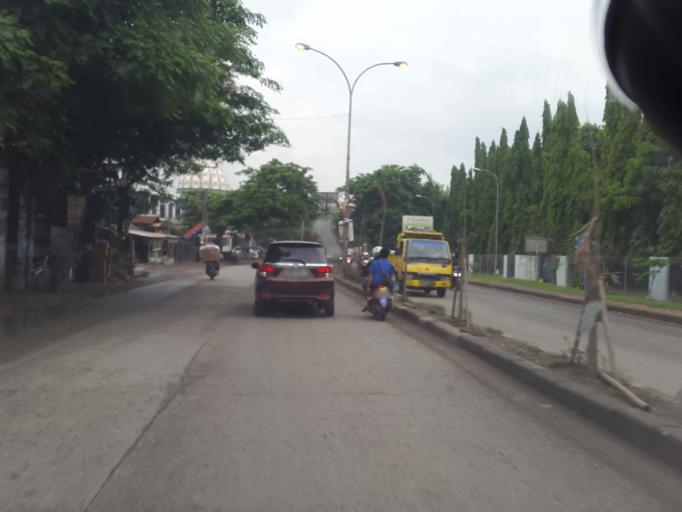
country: ID
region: West Java
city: Cikarang
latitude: -6.3040
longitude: 107.1448
